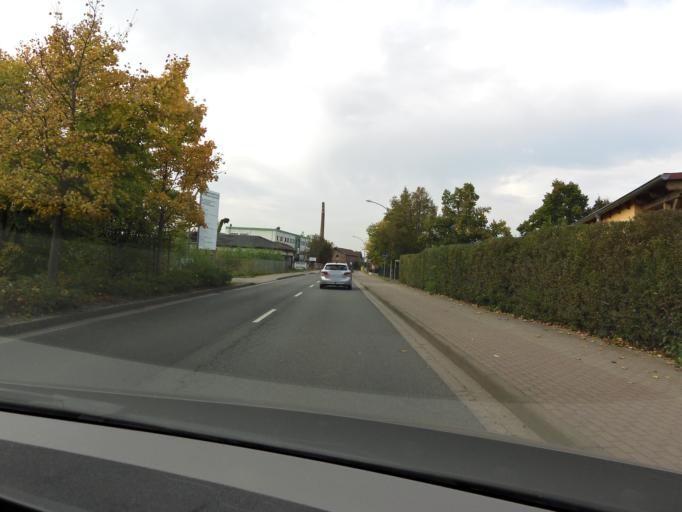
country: DE
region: Thuringia
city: Barchfeld
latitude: 50.7933
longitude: 10.3030
